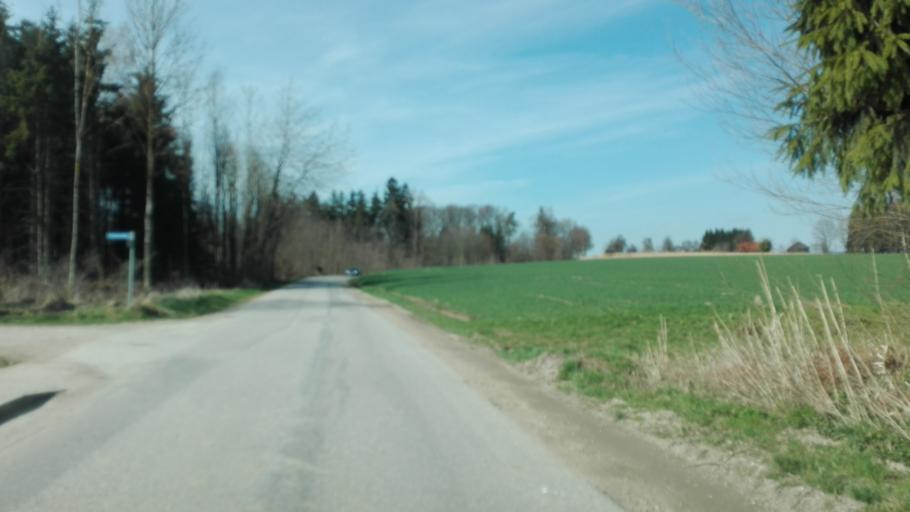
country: AT
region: Lower Austria
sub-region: Politischer Bezirk Amstetten
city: Ennsdorf
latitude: 48.2509
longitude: 14.5202
